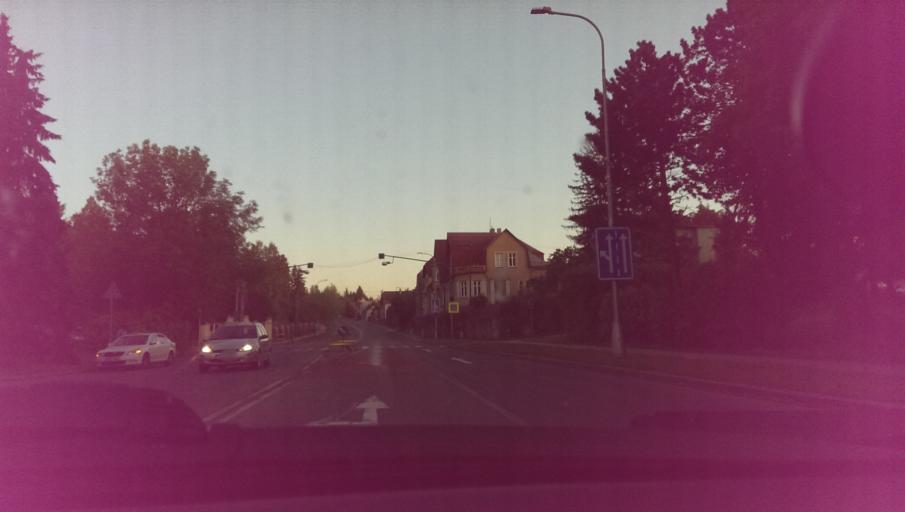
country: CZ
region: Zlin
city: Valasske Mezirici
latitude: 49.4685
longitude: 17.9734
